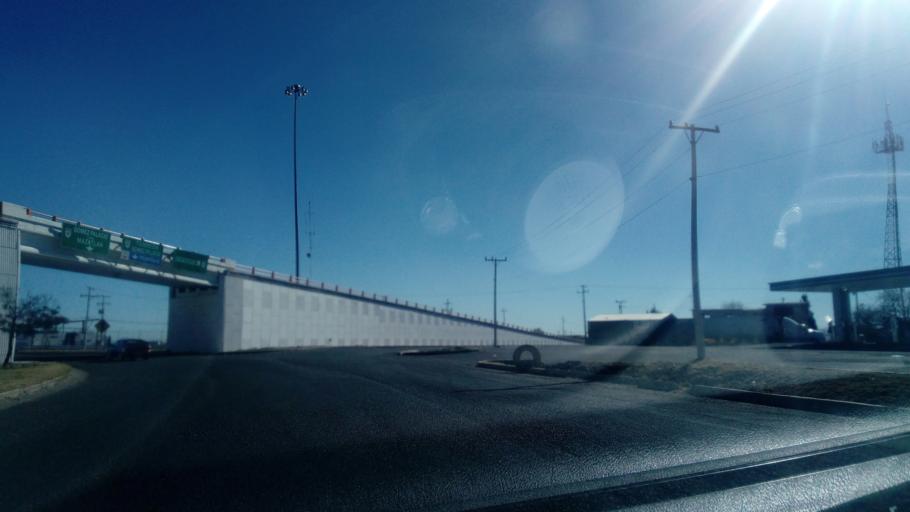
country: MX
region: Durango
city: Victoria de Durango
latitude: 24.0943
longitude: -104.5754
